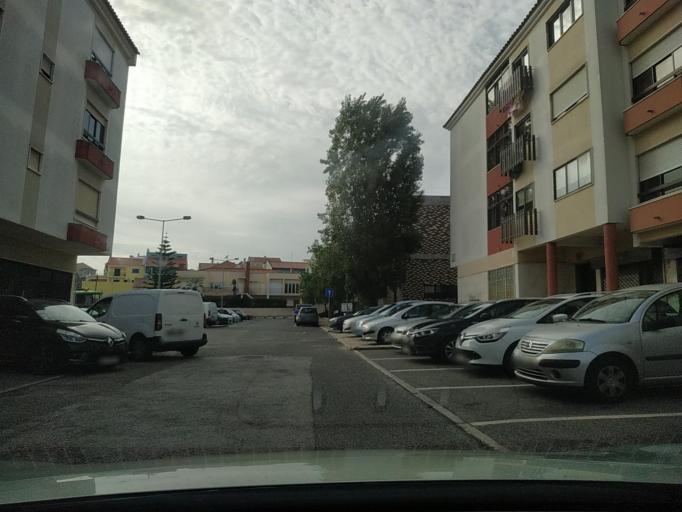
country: PT
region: Lisbon
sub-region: Odivelas
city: Famoes
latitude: 38.7783
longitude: -9.2316
